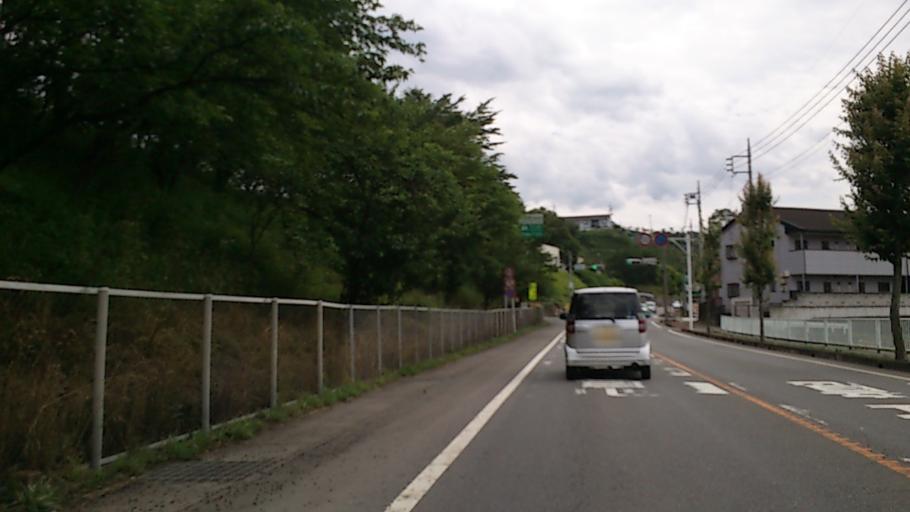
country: JP
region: Gunma
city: Tomioka
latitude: 36.2352
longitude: 138.8225
